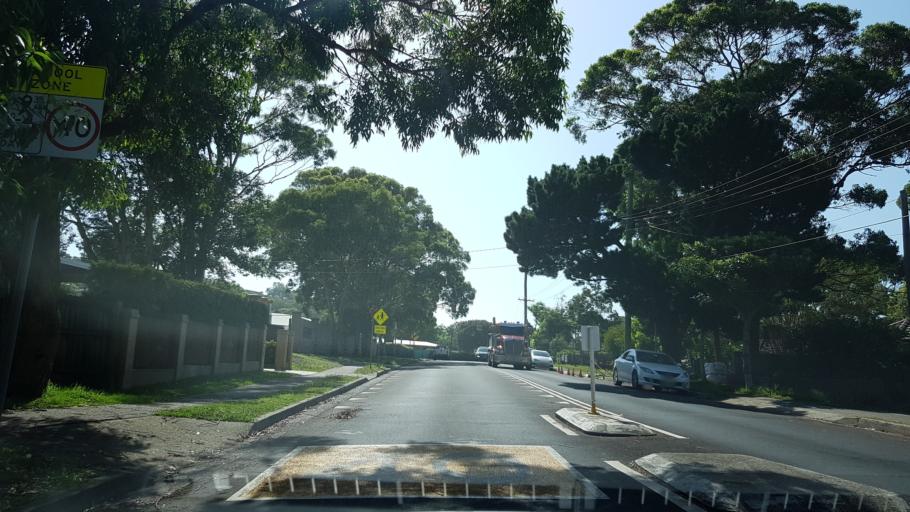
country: AU
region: New South Wales
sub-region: Warringah
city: Dee Why
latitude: -33.7413
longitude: 151.2897
